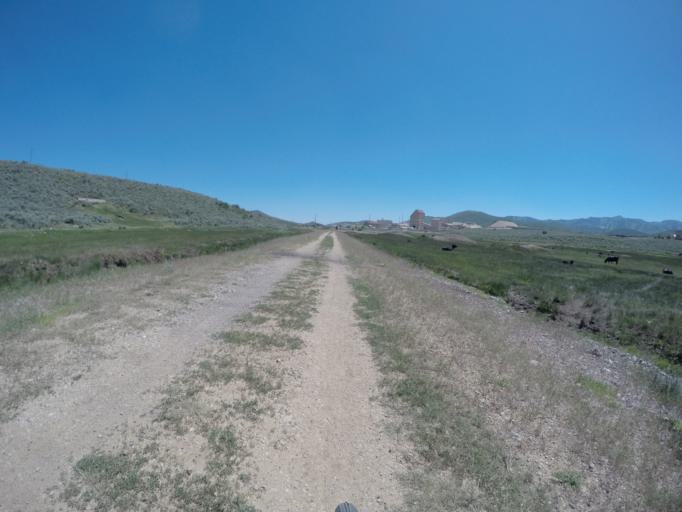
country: US
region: Utah
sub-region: Summit County
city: Park City
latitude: 40.6929
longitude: -111.4602
